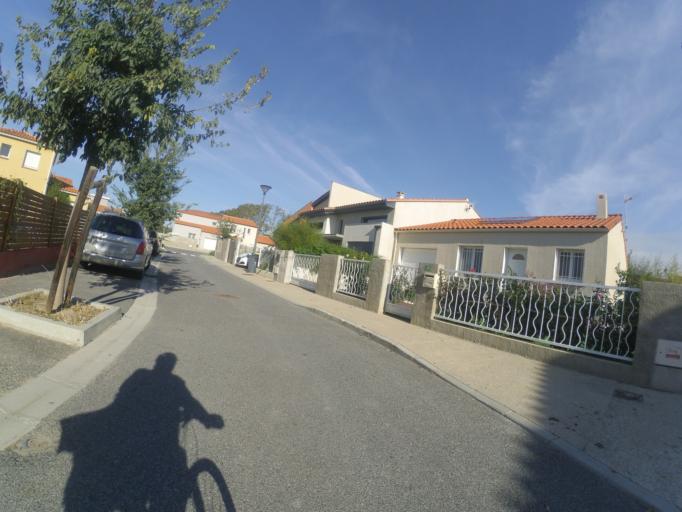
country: FR
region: Languedoc-Roussillon
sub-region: Departement des Pyrenees-Orientales
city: Pezilla-la-Riviere
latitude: 42.6943
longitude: 2.7618
